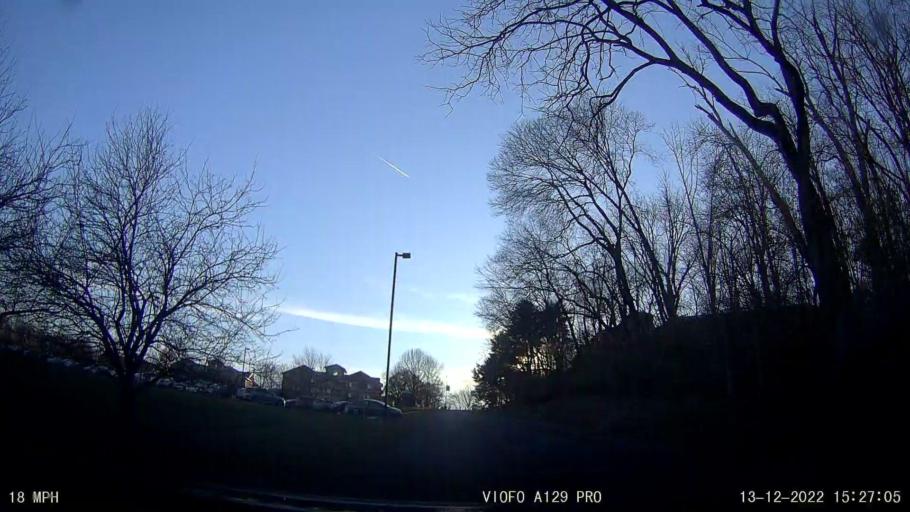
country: US
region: Pennsylvania
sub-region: Berks County
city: Spring Ridge
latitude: 40.3585
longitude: -75.9687
